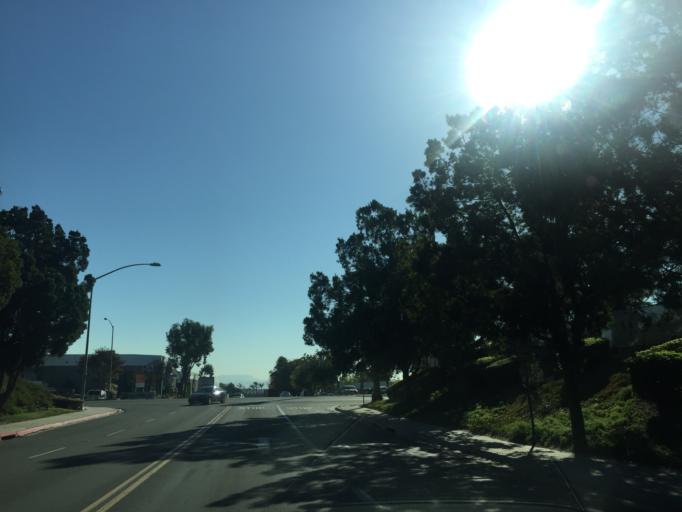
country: MX
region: Baja California
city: Tijuana
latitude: 32.5575
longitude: -116.9320
